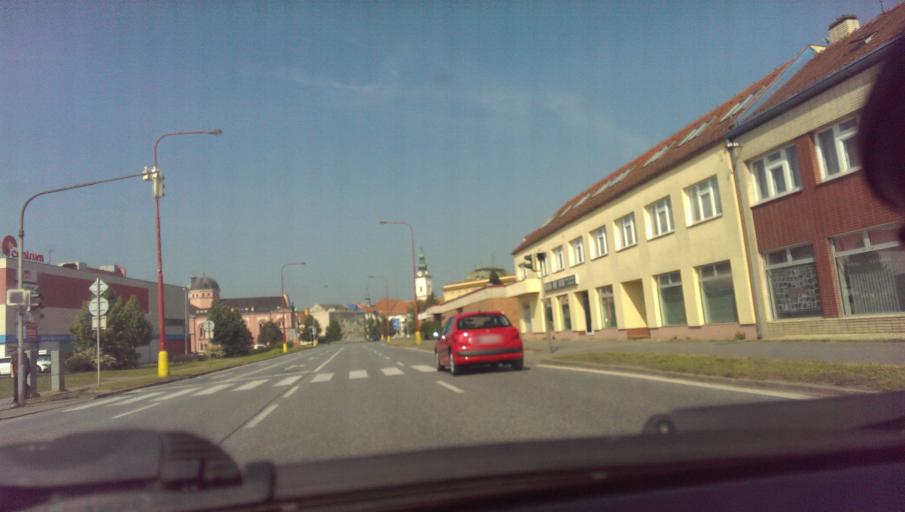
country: CZ
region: Zlin
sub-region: Okres Uherske Hradiste
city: Uherske Hradiste
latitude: 49.0706
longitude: 17.4644
